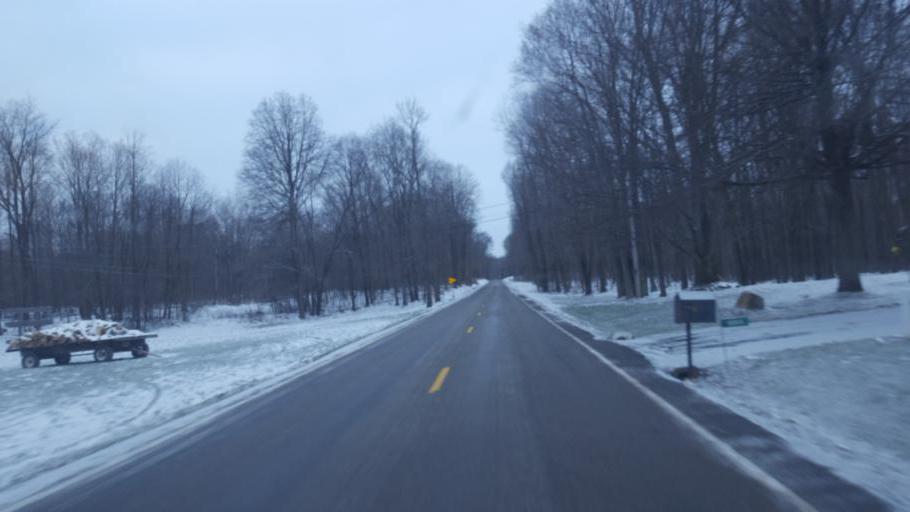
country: US
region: Pennsylvania
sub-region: Mercer County
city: Stoneboro
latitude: 41.4090
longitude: -80.0618
